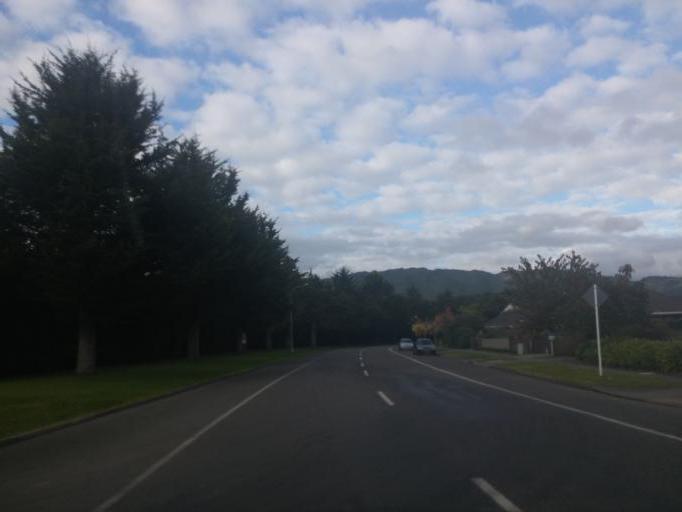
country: NZ
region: Wellington
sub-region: Kapiti Coast District
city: Paraparaumu
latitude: -40.8712
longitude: 175.0426
